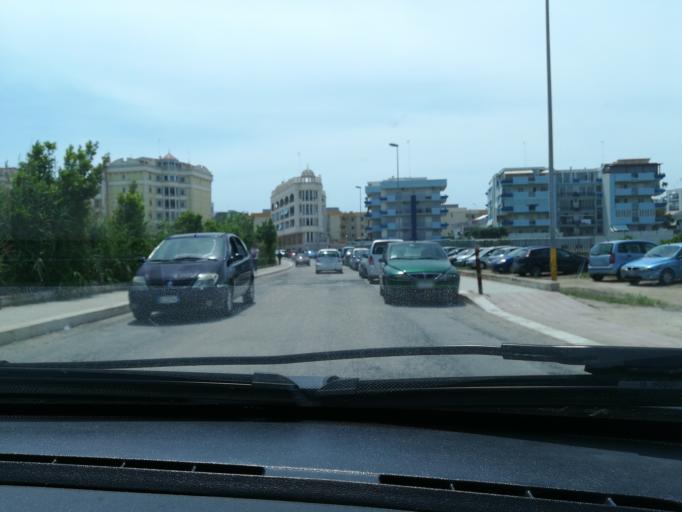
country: IT
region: Apulia
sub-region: Provincia di Barletta - Andria - Trani
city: Barletta
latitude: 41.3251
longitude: 16.2668
